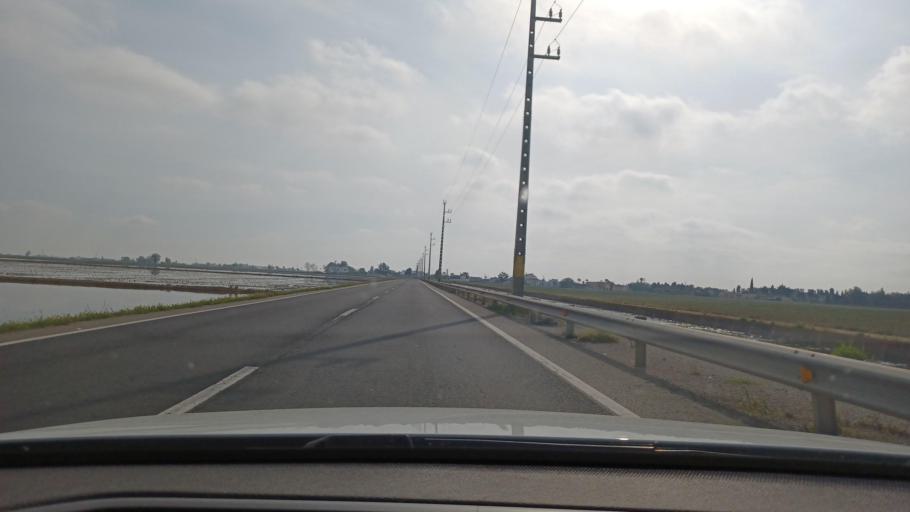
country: ES
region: Catalonia
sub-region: Provincia de Tarragona
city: Deltebre
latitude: 40.7258
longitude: 0.6709
